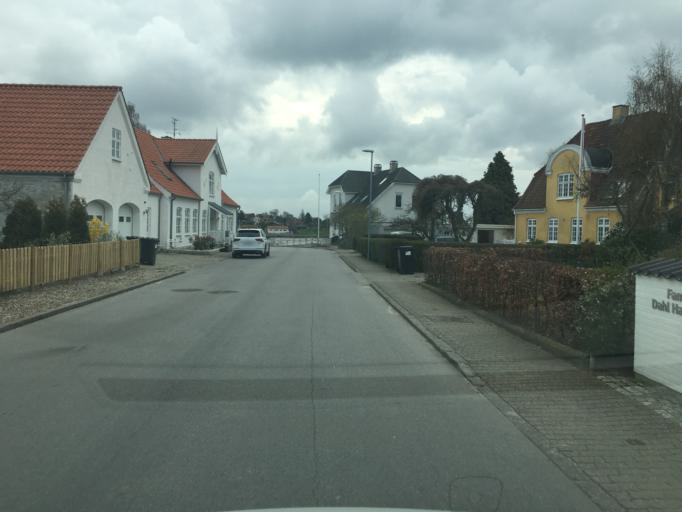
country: DK
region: South Denmark
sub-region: Sonderborg Kommune
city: Grasten
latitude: 54.9070
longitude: 9.5933
